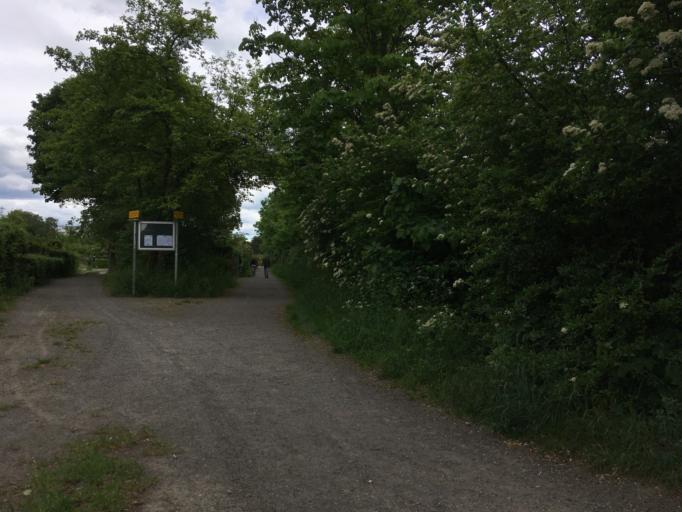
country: DE
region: Berlin
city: Friedrichsfelde
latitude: 52.5147
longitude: 13.5136
